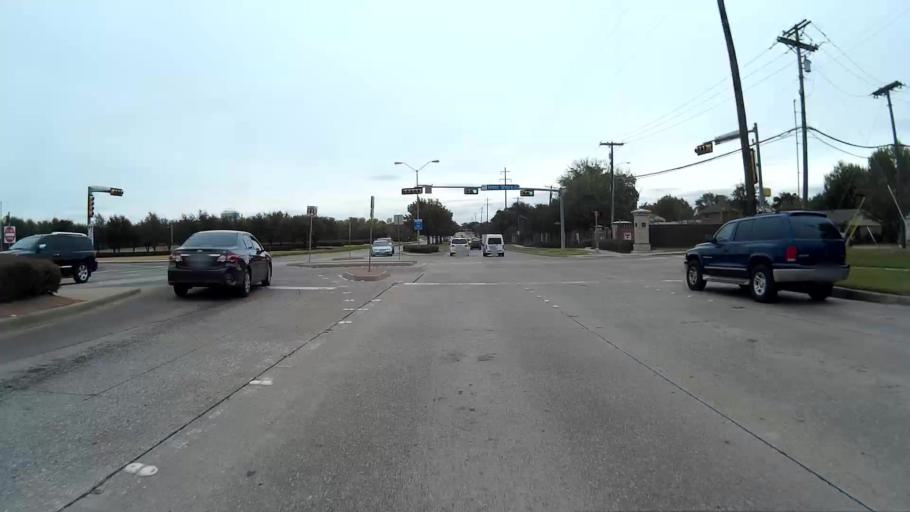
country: US
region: Texas
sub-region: Dallas County
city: Richardson
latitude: 32.9781
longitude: -96.7484
